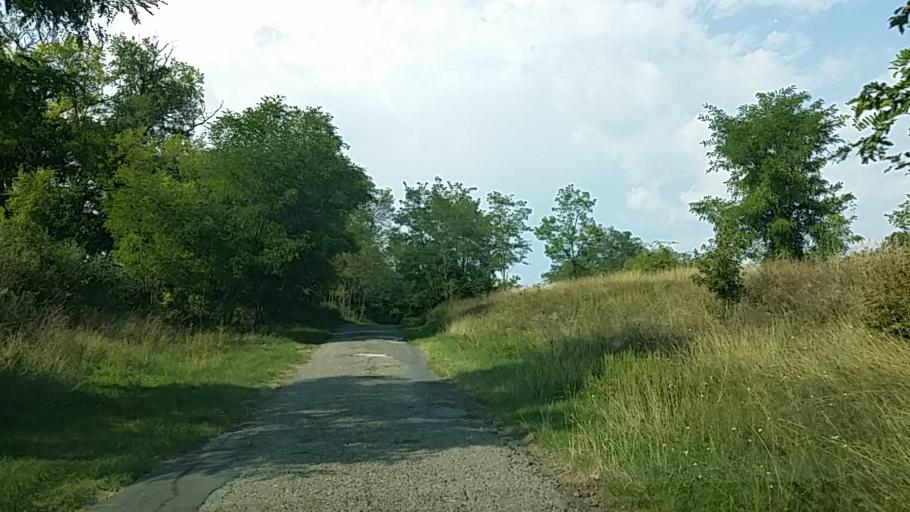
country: HU
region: Nograd
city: Bujak
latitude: 47.8696
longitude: 19.5006
